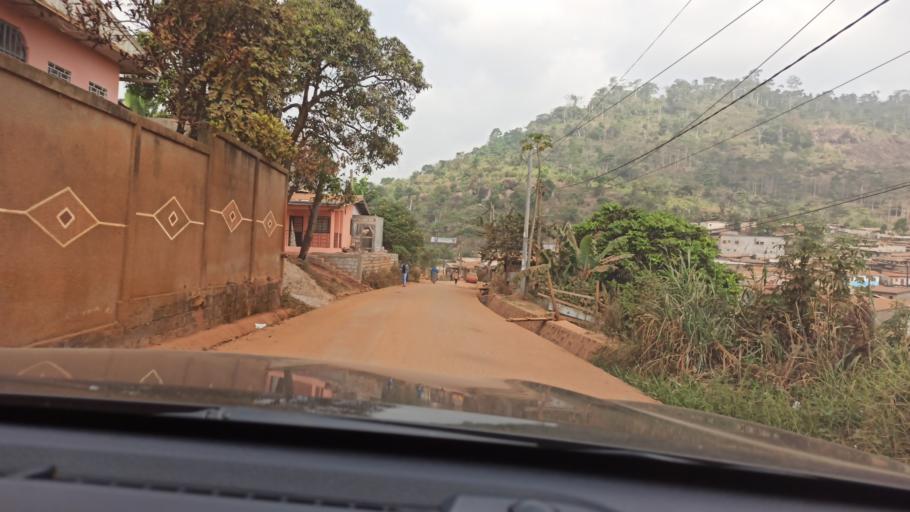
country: CM
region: Centre
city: Yaounde
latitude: 3.8791
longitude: 11.4799
